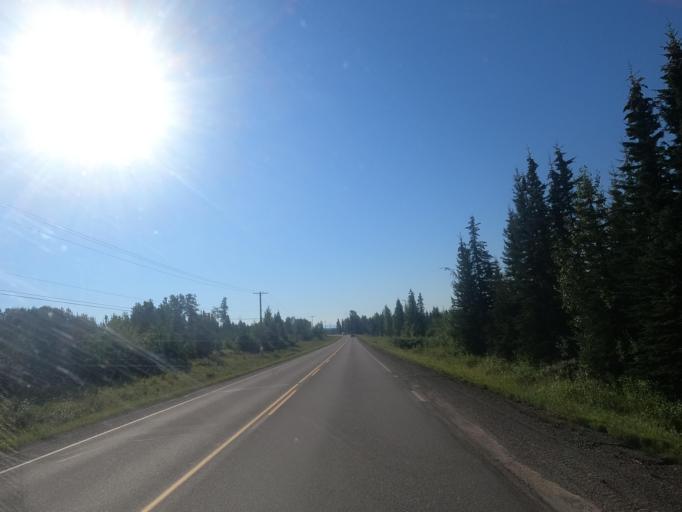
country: CA
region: British Columbia
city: Burns Lake
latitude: 54.3513
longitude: -125.9145
